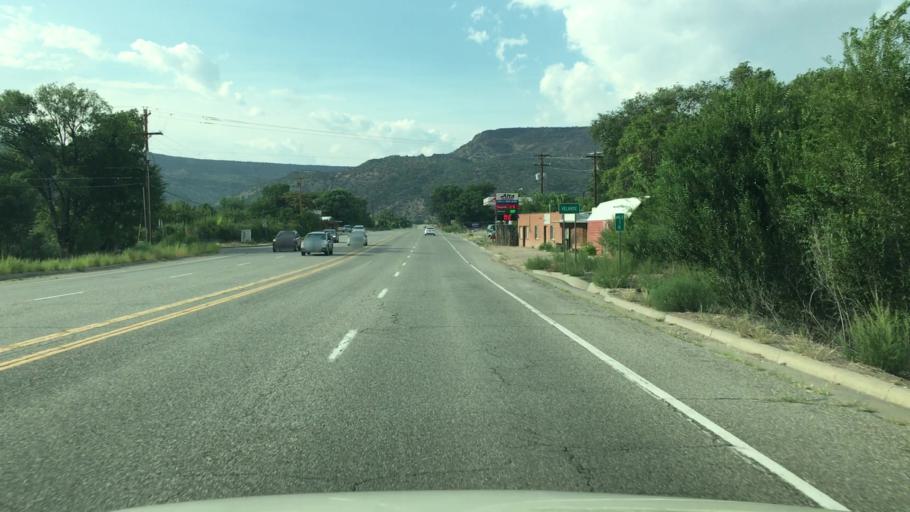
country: US
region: New Mexico
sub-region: Rio Arriba County
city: Ohkay Owingeh
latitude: 36.1637
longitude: -105.9674
